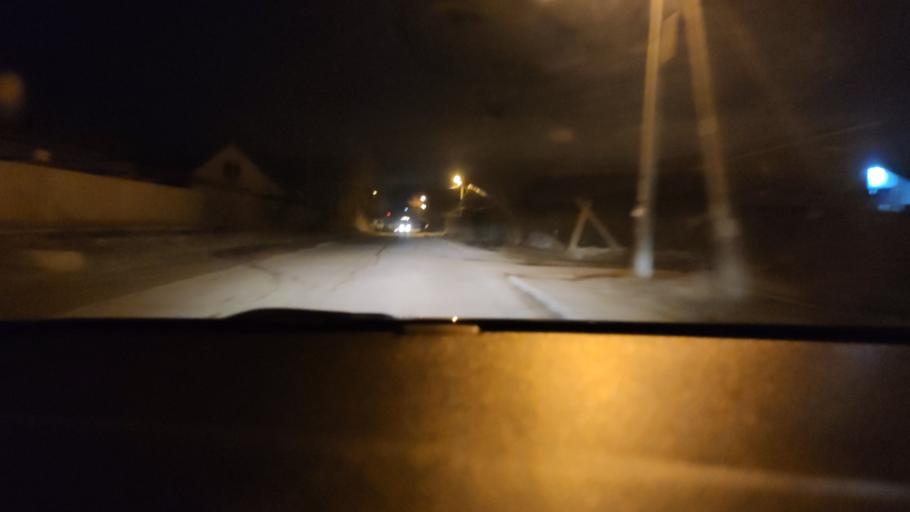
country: RU
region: Tatarstan
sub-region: Gorod Kazan'
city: Kazan
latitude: 55.8451
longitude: 49.1993
